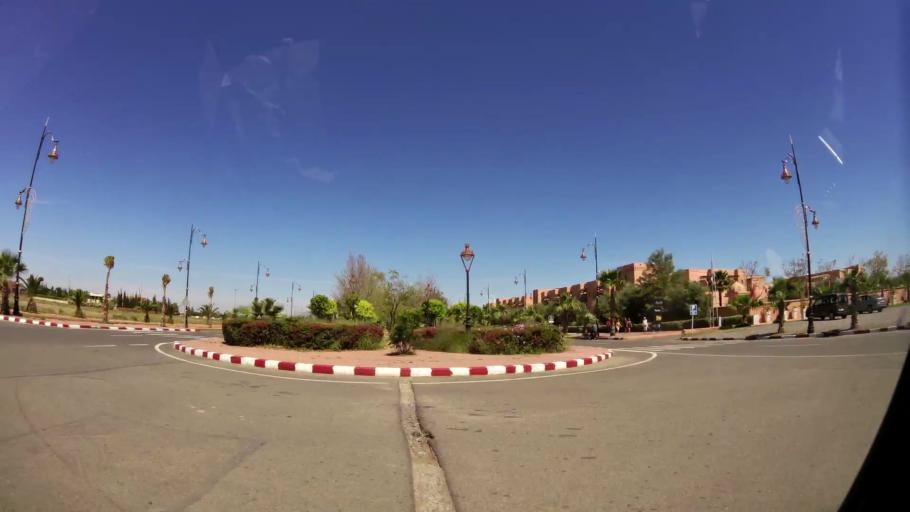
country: MA
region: Marrakech-Tensift-Al Haouz
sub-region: Marrakech
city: Marrakesh
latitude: 31.5919
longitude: -7.9911
